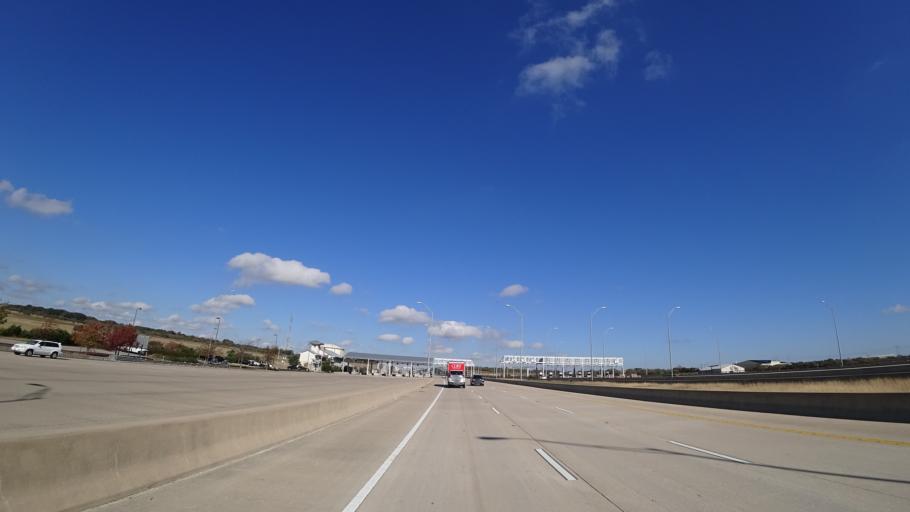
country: US
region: Texas
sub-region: Travis County
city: Wells Branch
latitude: 30.4517
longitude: -97.6966
